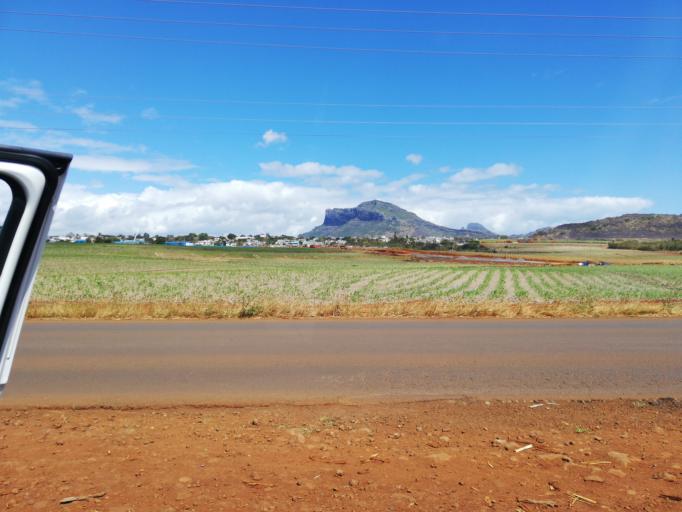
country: MU
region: Black River
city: Petite Riviere
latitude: -20.2145
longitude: 57.4569
